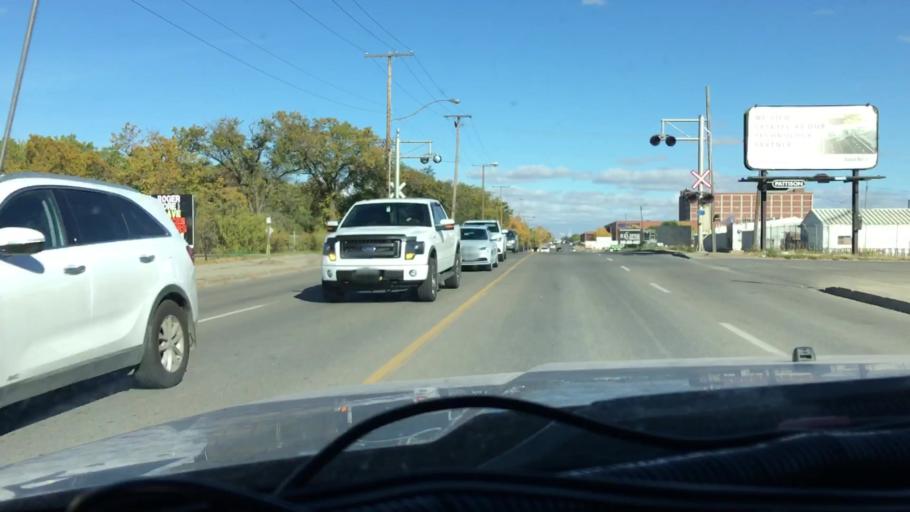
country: CA
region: Saskatchewan
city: Regina
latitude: 50.4629
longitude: -104.6161
